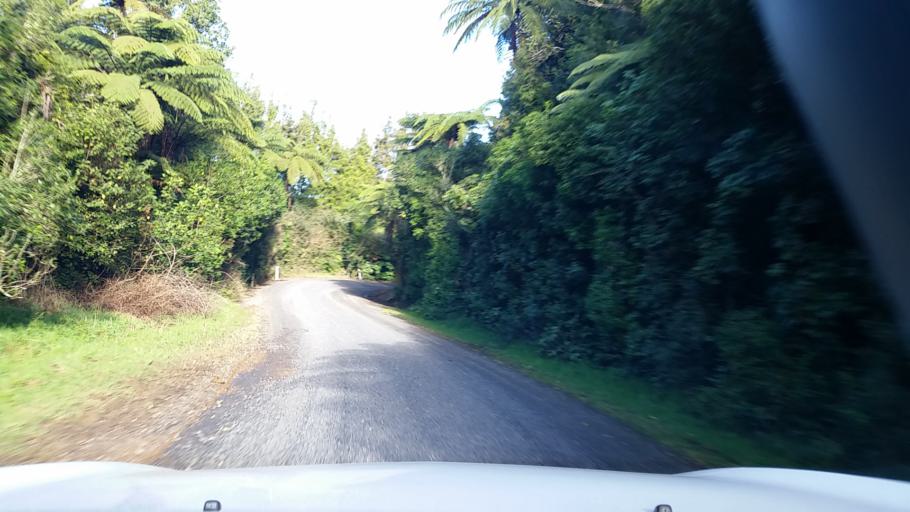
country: NZ
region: Waikato
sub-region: Matamata-Piako District
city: Matamata
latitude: -37.8161
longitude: 175.6328
